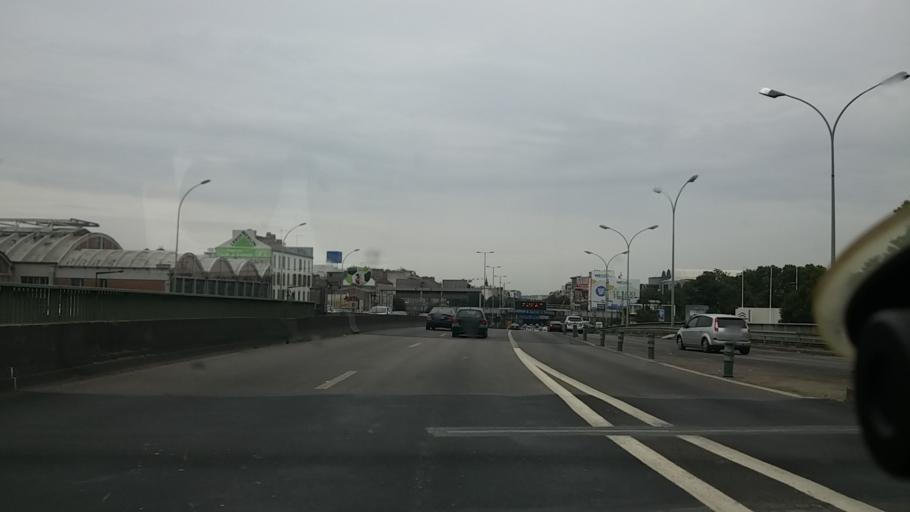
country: FR
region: Ile-de-France
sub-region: Paris
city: Saint-Ouen
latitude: 48.9018
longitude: 2.3589
